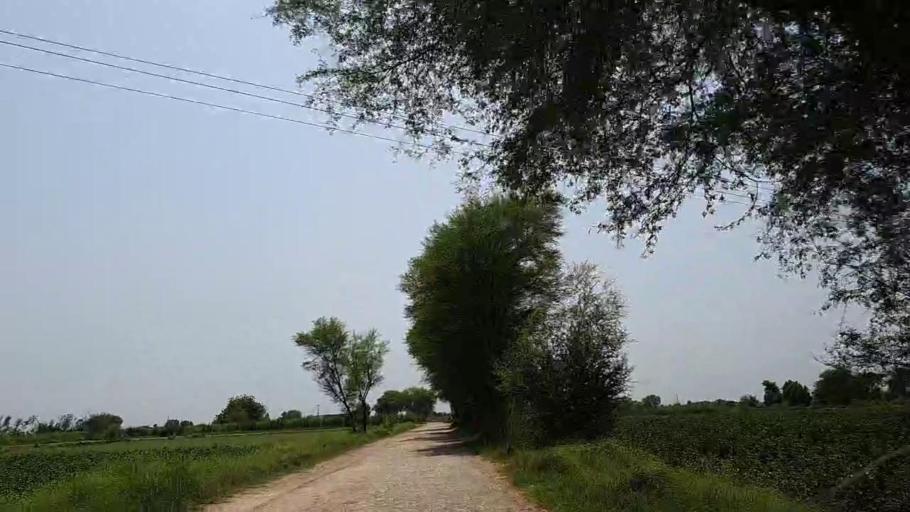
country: PK
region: Sindh
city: Ghotki
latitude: 27.9747
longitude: 69.3998
